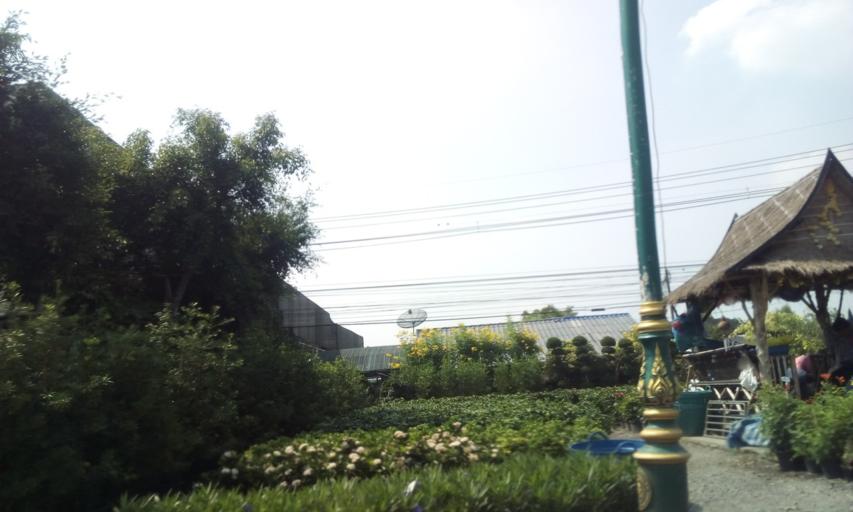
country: TH
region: Nakhon Nayok
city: Ongkharak
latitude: 14.1072
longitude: 100.9436
